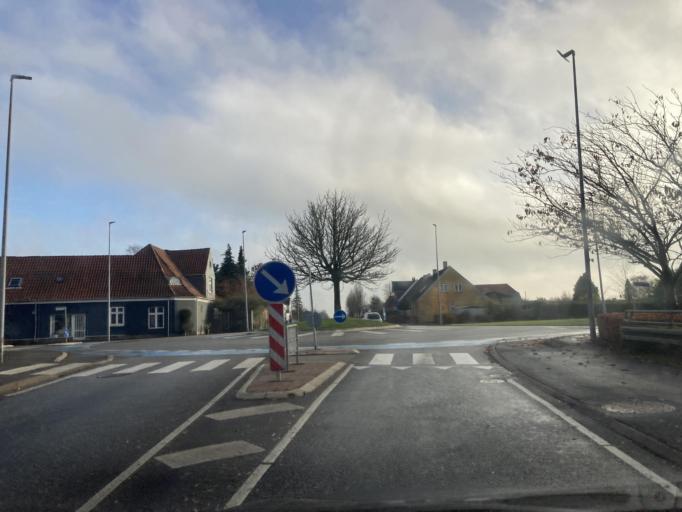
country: DK
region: Zealand
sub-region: Lolland Kommune
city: Maribo
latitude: 54.8067
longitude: 11.4296
